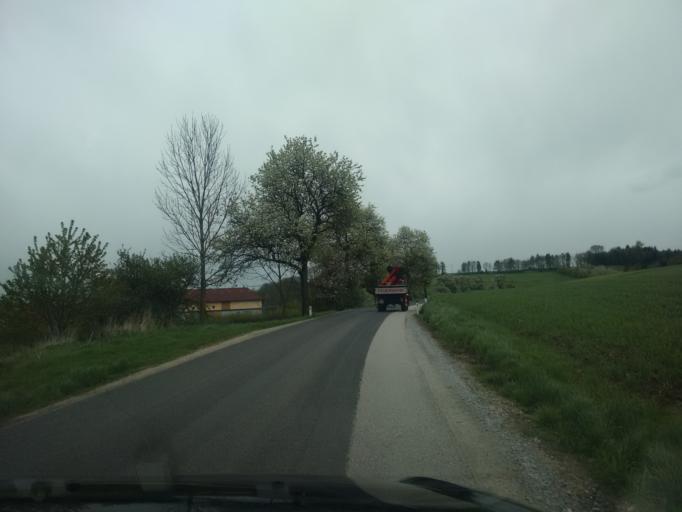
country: AT
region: Upper Austria
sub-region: Wels-Land
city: Buchkirchen
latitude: 48.2085
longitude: 13.9973
